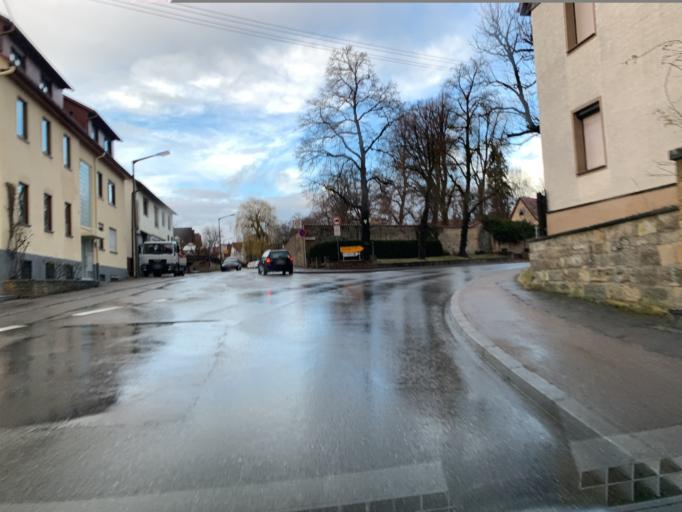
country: DE
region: Baden-Wuerttemberg
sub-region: Regierungsbezirk Stuttgart
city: Magstadt
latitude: 48.7449
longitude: 8.9634
